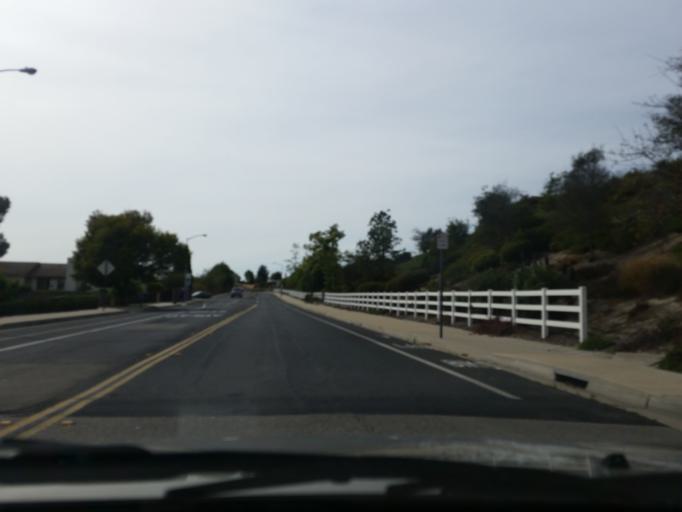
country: US
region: California
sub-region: San Luis Obispo County
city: Arroyo Grande
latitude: 35.1323
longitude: -120.5781
